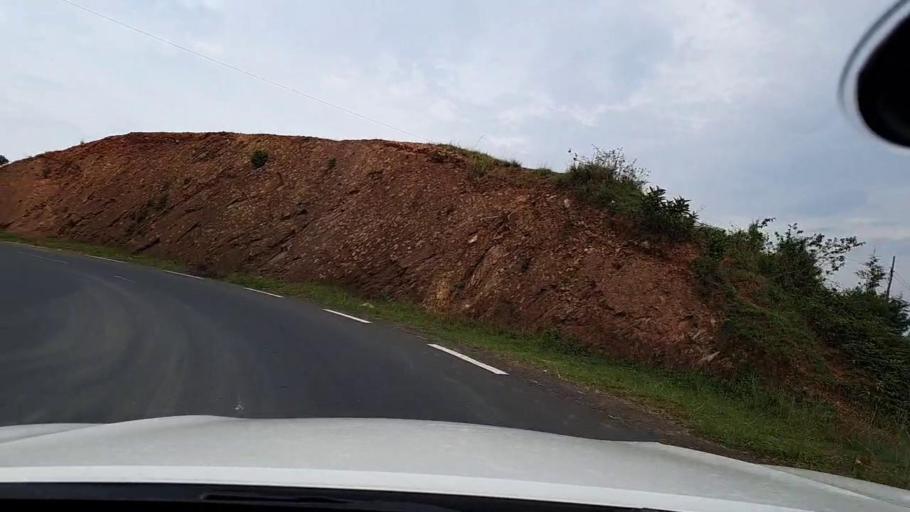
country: RW
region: Western Province
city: Kibuye
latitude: -2.1680
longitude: 29.2903
